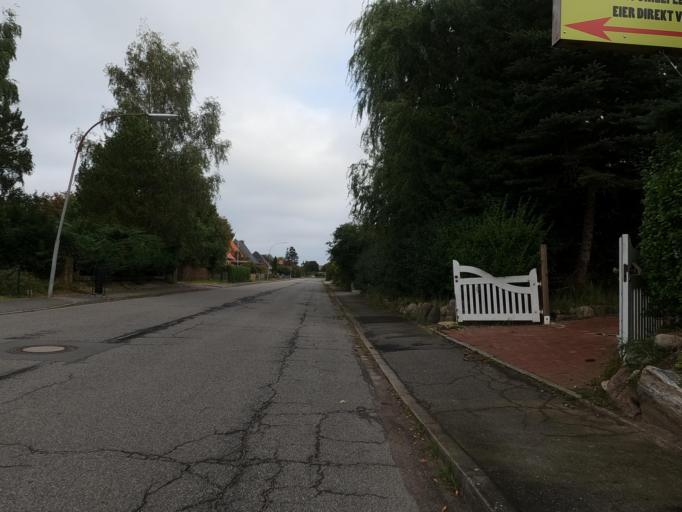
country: DE
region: Schleswig-Holstein
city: Grube
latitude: 54.2711
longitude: 11.0531
